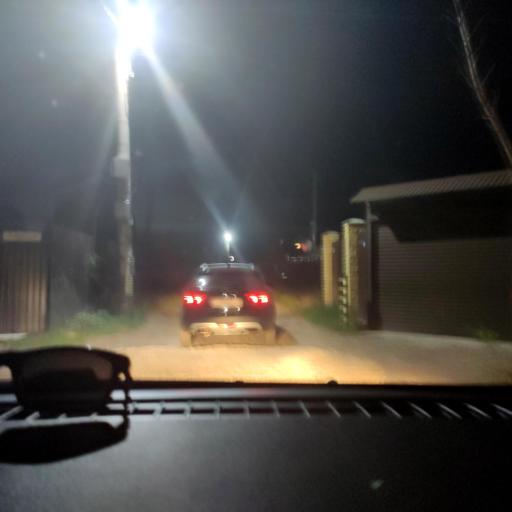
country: RU
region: Samara
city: Volzhskiy
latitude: 53.4474
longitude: 50.0746
